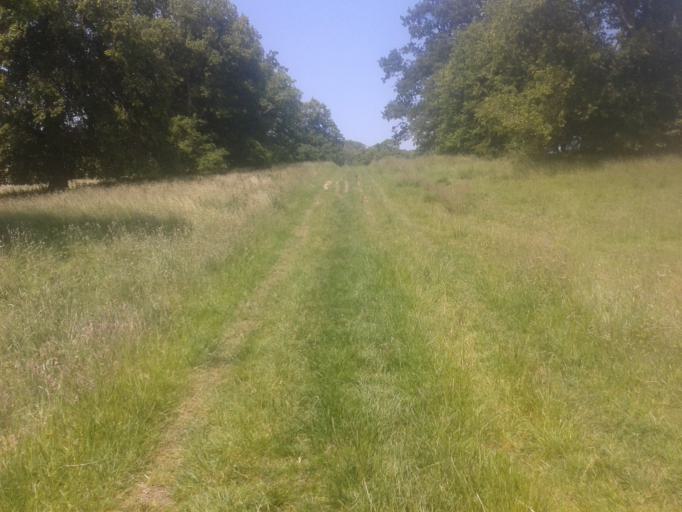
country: GB
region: England
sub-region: East Riding of Yorkshire
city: Londesborough
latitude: 53.8952
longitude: -0.6727
